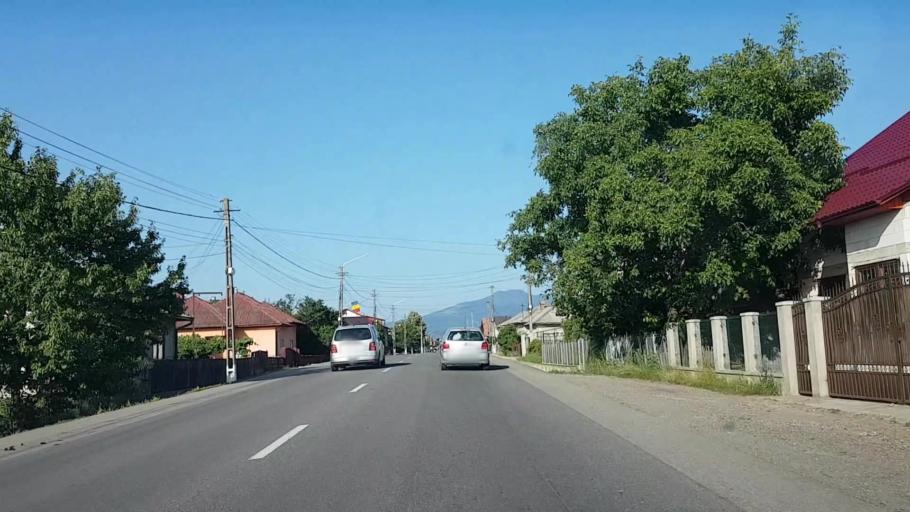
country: RO
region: Bistrita-Nasaud
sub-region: Comuna Josenii Bargaului
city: Josenii Bargaului
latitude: 47.2126
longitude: 24.6826
